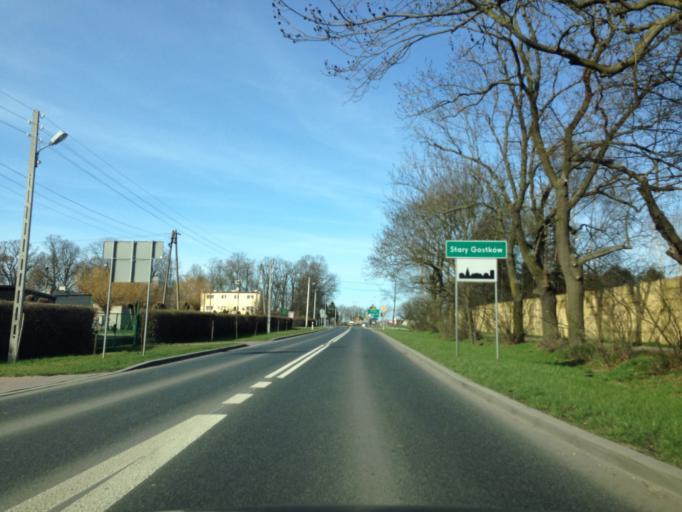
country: PL
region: Lodz Voivodeship
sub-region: Powiat poddebicki
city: Wartkowice
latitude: 51.9706
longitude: 19.0170
